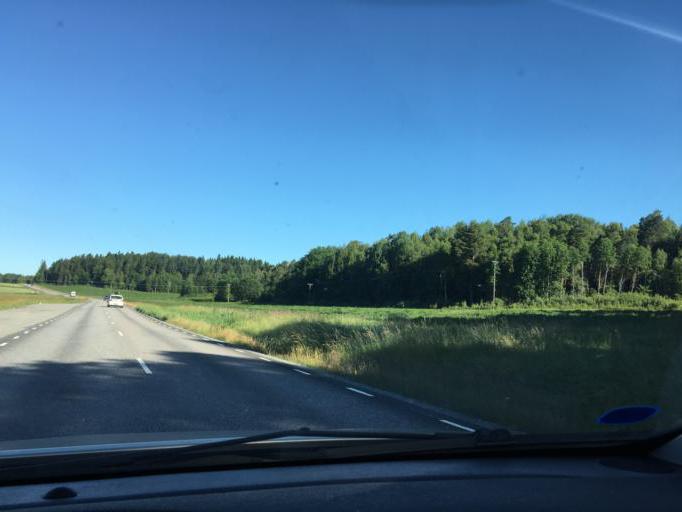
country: SE
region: Stockholm
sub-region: Salems Kommun
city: Ronninge
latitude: 59.2254
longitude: 17.7343
